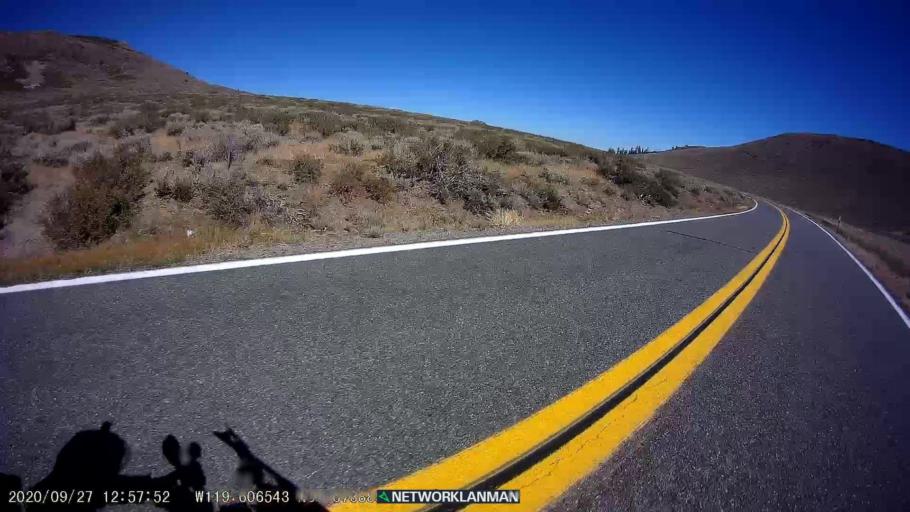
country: US
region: Nevada
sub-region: Douglas County
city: Gardnerville Ranchos
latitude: 38.6739
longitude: -119.6065
